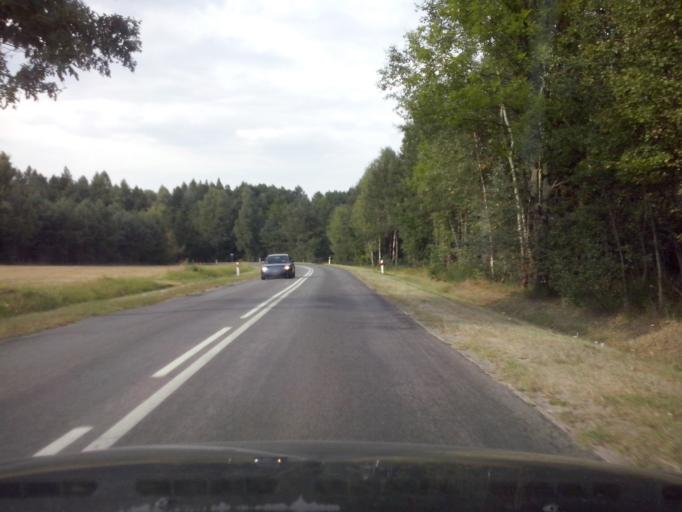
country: PL
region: Swietokrzyskie
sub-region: Powiat kielecki
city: Rakow
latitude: 50.6550
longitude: 21.0719
